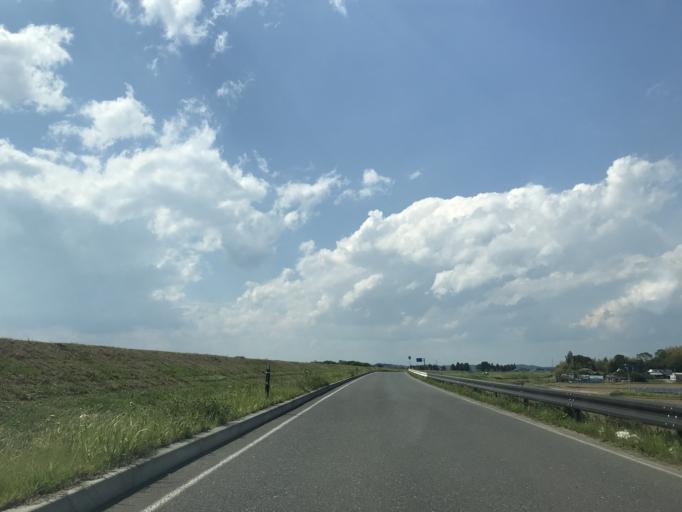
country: JP
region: Miyagi
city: Matsushima
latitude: 38.4363
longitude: 141.1189
